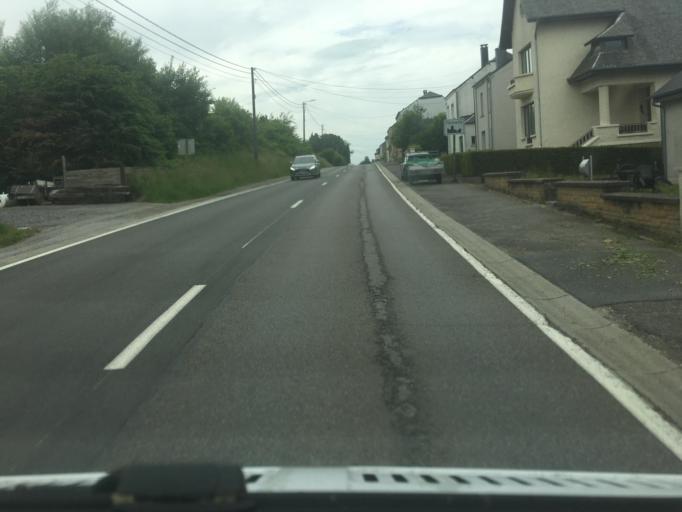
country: BE
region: Wallonia
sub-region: Province du Luxembourg
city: Florenville
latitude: 49.7005
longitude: 5.3214
